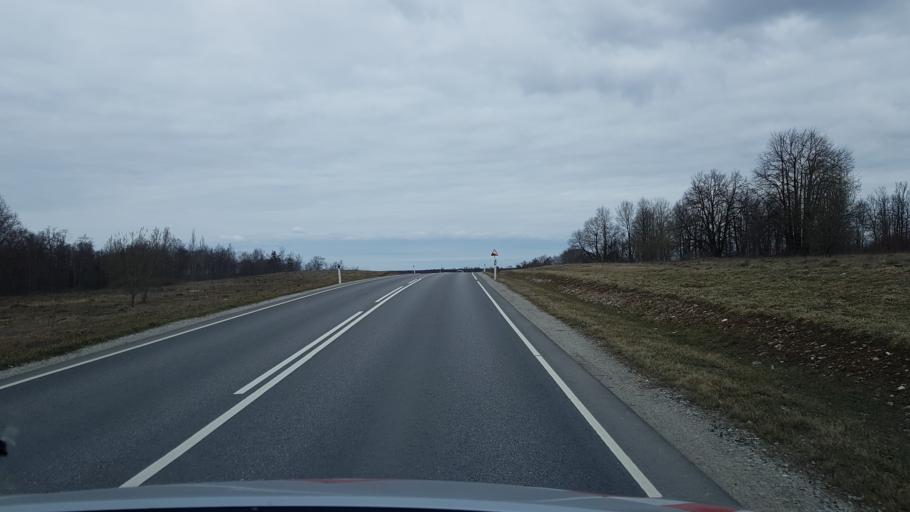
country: EE
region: Ida-Virumaa
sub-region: Narva-Joesuu linn
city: Narva-Joesuu
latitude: 59.4057
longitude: 28.0668
